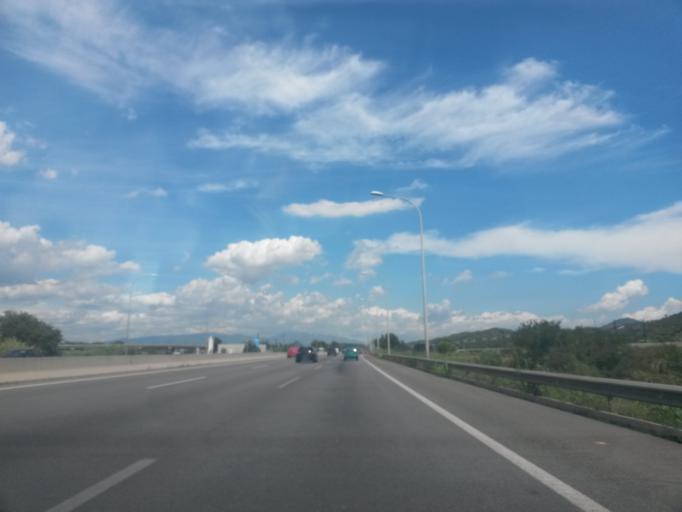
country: ES
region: Catalonia
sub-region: Provincia de Barcelona
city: La Llagosta
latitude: 41.5012
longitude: 2.1951
